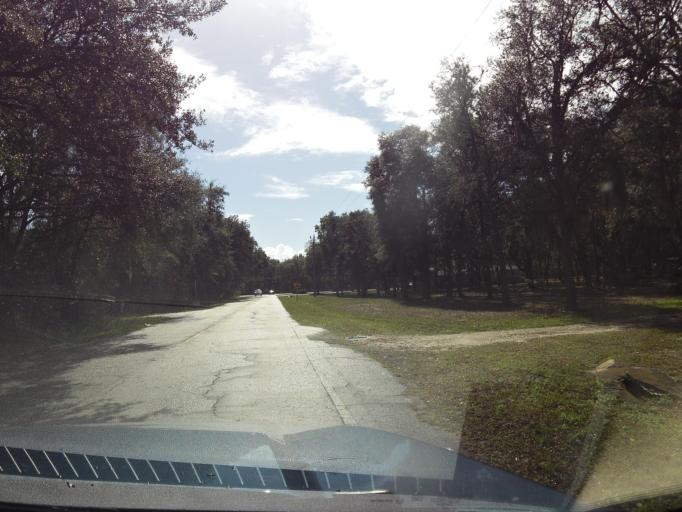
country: US
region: Florida
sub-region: Clay County
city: Asbury Lake
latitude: 29.9839
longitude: -81.8396
